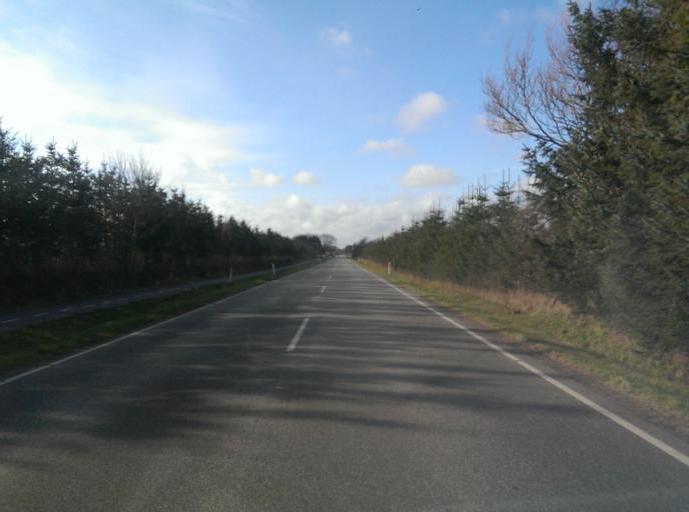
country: DK
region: South Denmark
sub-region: Esbjerg Kommune
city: Bramming
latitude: 55.4551
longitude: 8.7174
